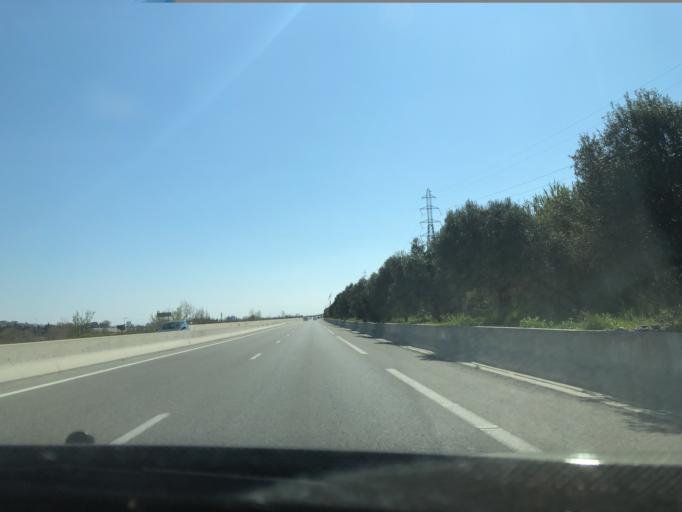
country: FR
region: Provence-Alpes-Cote d'Azur
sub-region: Departement des Alpes-Maritimes
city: La Gaude
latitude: 43.7102
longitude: 7.1837
